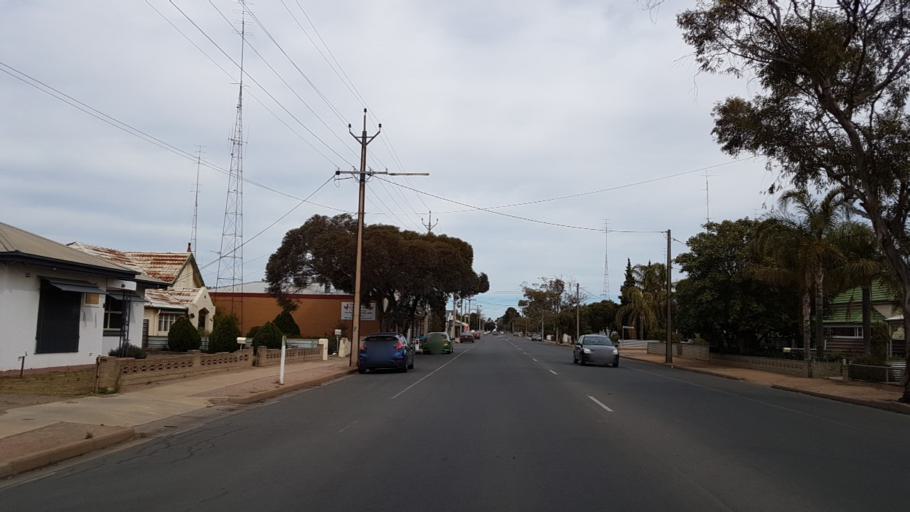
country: AU
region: South Australia
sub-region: Port Pirie City and Dists
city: Port Pirie
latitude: -33.1916
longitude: 138.0039
